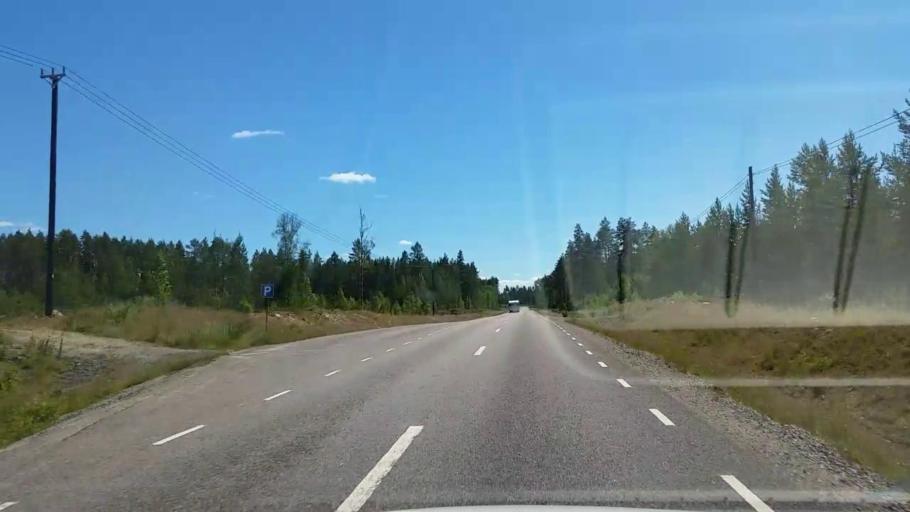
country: SE
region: Gaevleborg
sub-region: Ovanakers Kommun
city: Edsbyn
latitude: 61.4642
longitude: 15.6983
